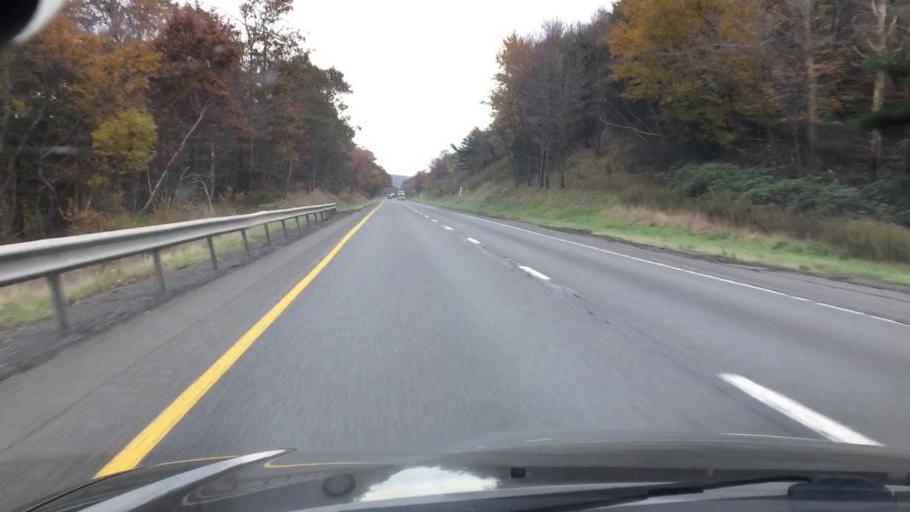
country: US
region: Pennsylvania
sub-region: Monroe County
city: Tannersville
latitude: 41.0642
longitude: -75.3489
